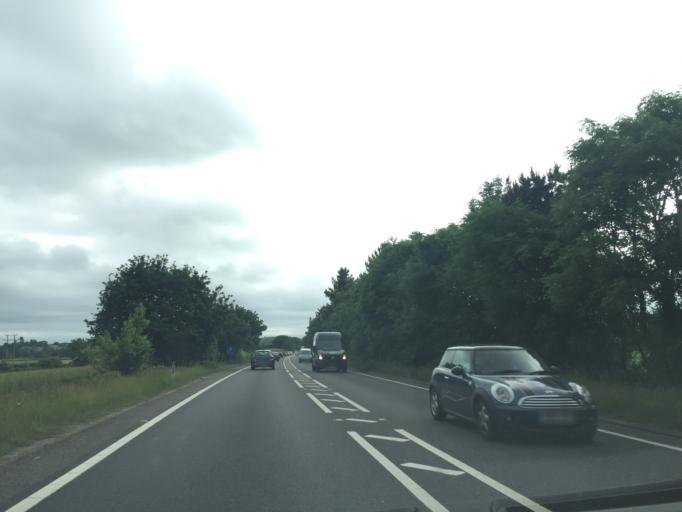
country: GB
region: England
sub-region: Dorset
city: Wimborne Minster
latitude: 50.7996
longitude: -1.9429
